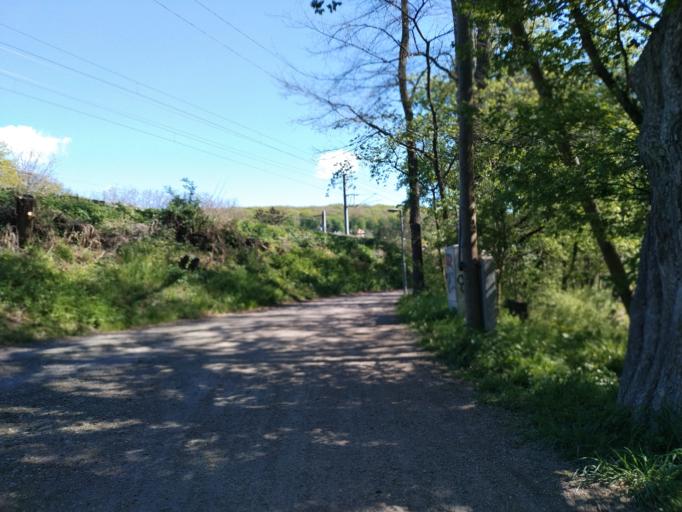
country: AT
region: Lower Austria
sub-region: Politischer Bezirk Wien-Umgebung
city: Purkersdorf
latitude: 48.2084
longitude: 16.2075
